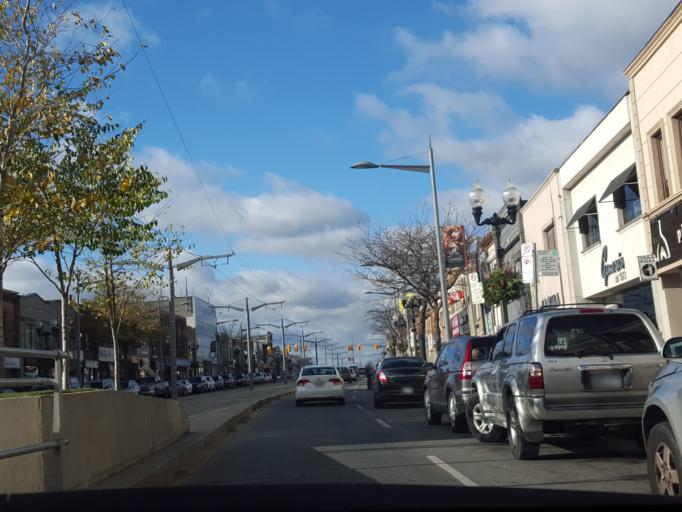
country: CA
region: Ontario
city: Toronto
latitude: 43.6778
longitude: -79.4437
